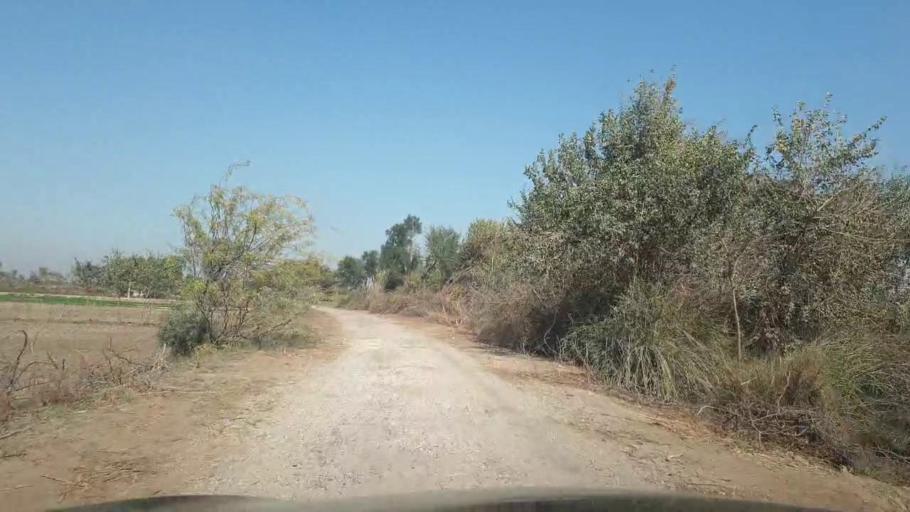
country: PK
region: Sindh
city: Ghotki
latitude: 27.9855
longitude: 69.4282
